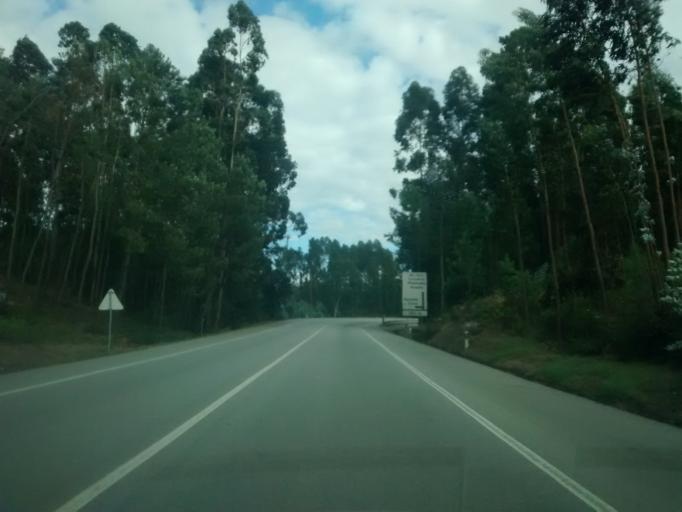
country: PT
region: Aveiro
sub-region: Agueda
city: Aguada de Cima
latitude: 40.5043
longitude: -8.4438
